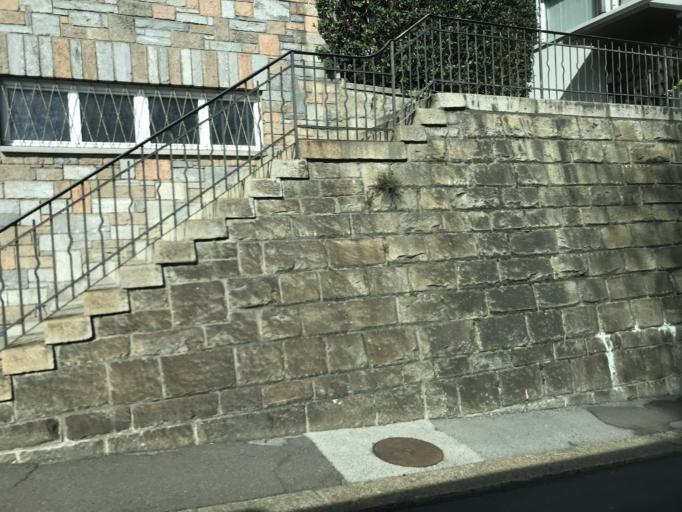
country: CH
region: Ticino
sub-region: Lugano District
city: Massagno
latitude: 46.0061
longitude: 8.9451
